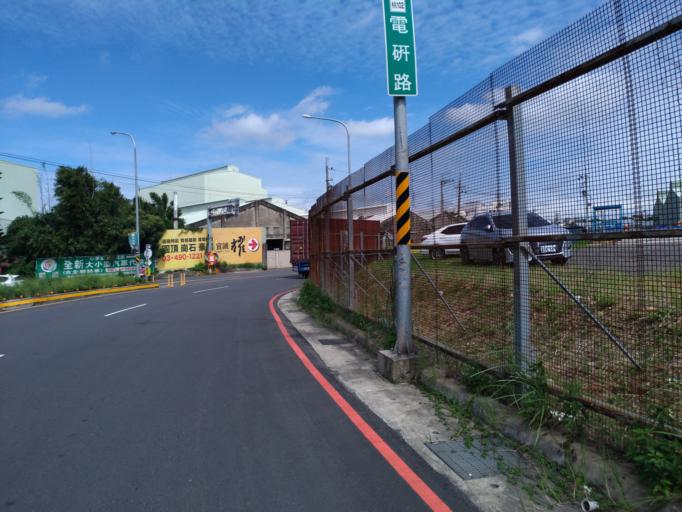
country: TW
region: Taiwan
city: Taoyuan City
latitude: 24.9485
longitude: 121.1647
